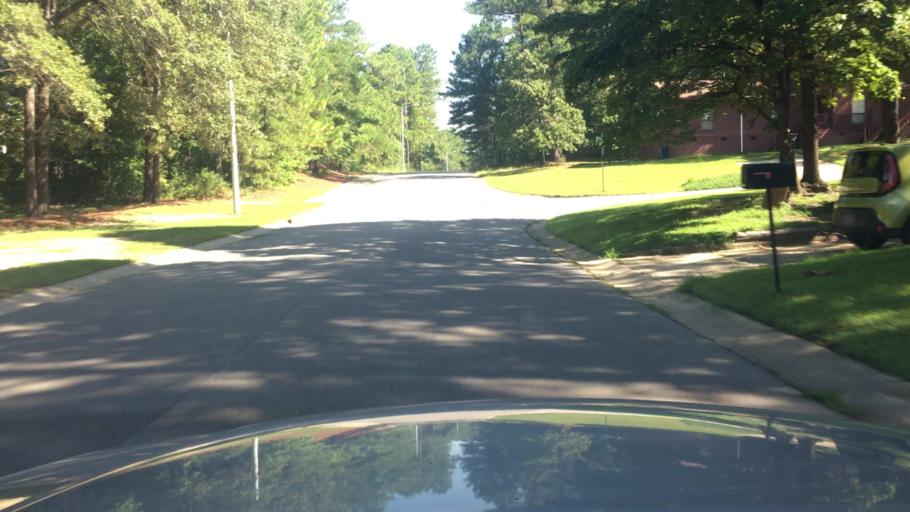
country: US
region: North Carolina
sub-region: Cumberland County
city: Fayetteville
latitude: 35.1095
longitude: -78.9107
